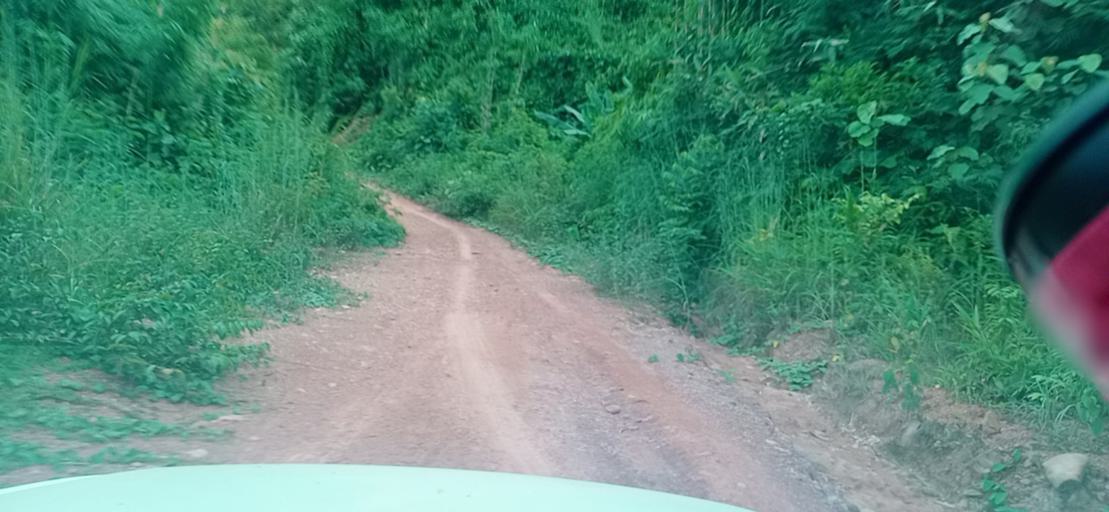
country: TH
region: Changwat Bueng Kan
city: Pak Khat
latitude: 18.5604
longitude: 103.2928
